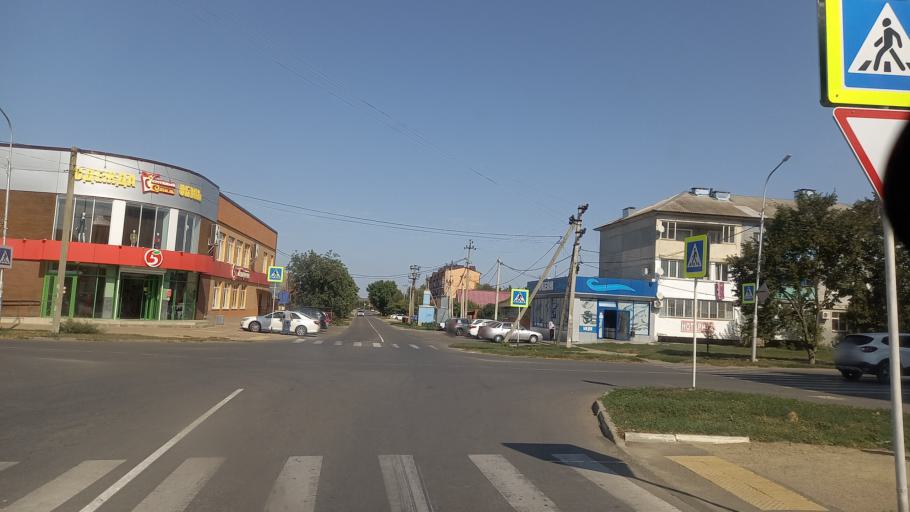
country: RU
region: Krasnodarskiy
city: Bryukhovetskaya
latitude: 45.8026
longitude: 38.9975
